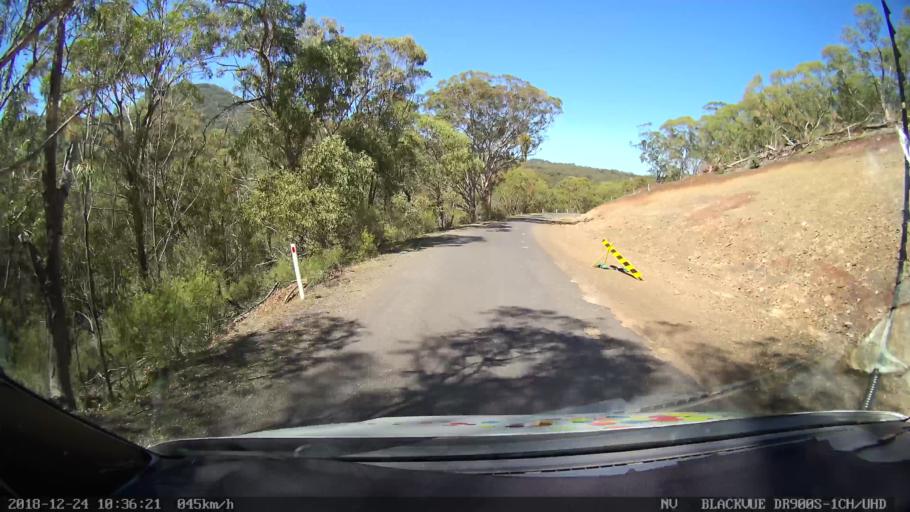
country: AU
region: New South Wales
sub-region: Upper Hunter Shire
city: Merriwa
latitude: -31.8440
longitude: 150.5002
